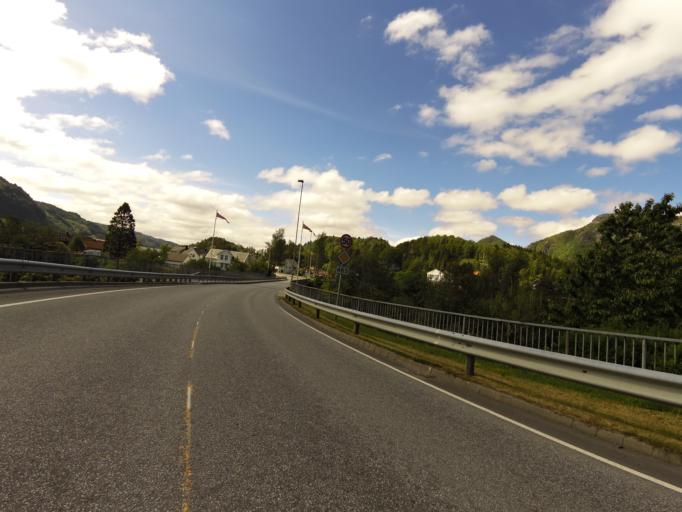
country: NO
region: Vest-Agder
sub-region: Kvinesdal
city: Liknes
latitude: 58.3120
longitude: 6.9617
